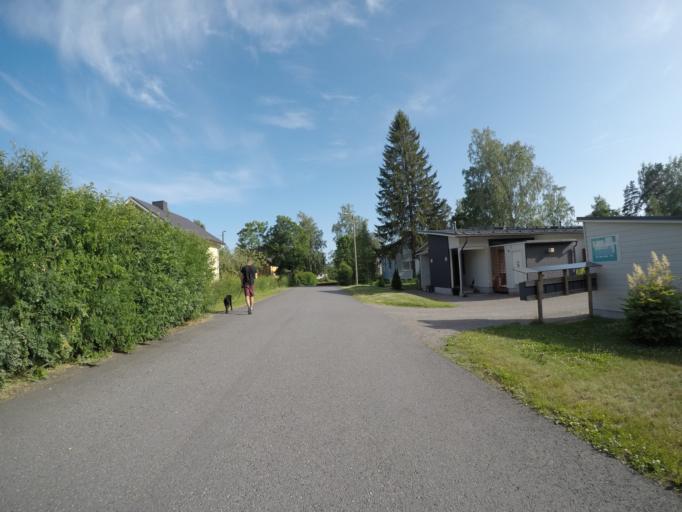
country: FI
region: Haeme
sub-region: Haemeenlinna
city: Haemeenlinna
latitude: 60.9803
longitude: 24.4157
